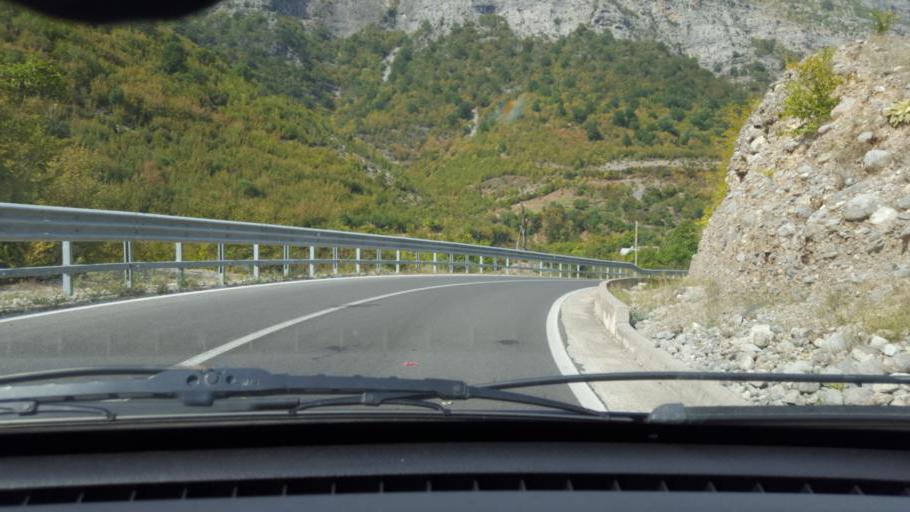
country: AL
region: Shkoder
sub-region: Rrethi i Malesia e Madhe
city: Kastrat
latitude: 42.4395
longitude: 19.5384
